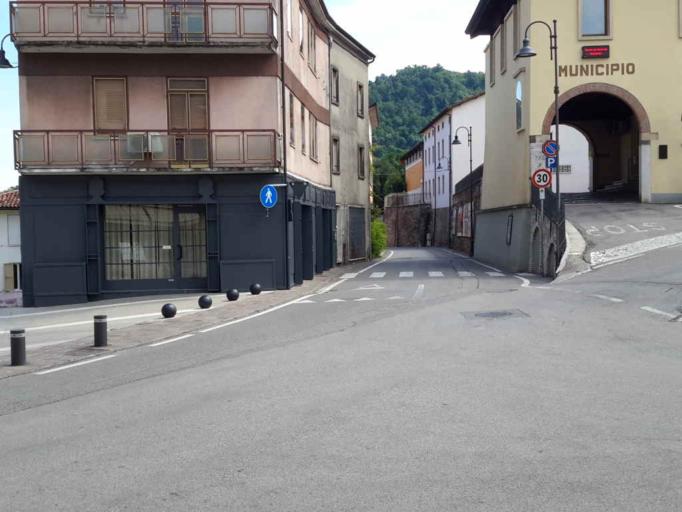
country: IT
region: Veneto
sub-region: Provincia di Vicenza
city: Montorso Vicentino
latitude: 45.4899
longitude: 11.3622
